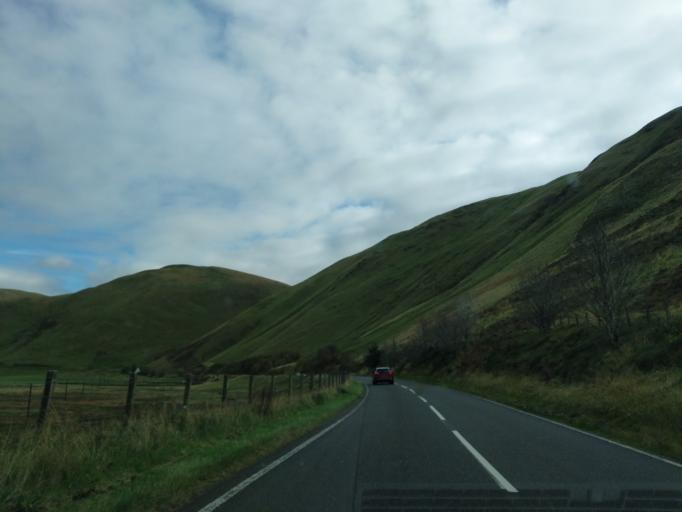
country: GB
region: Scotland
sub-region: Dumfries and Galloway
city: Thornhill
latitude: 55.3434
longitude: -3.7517
